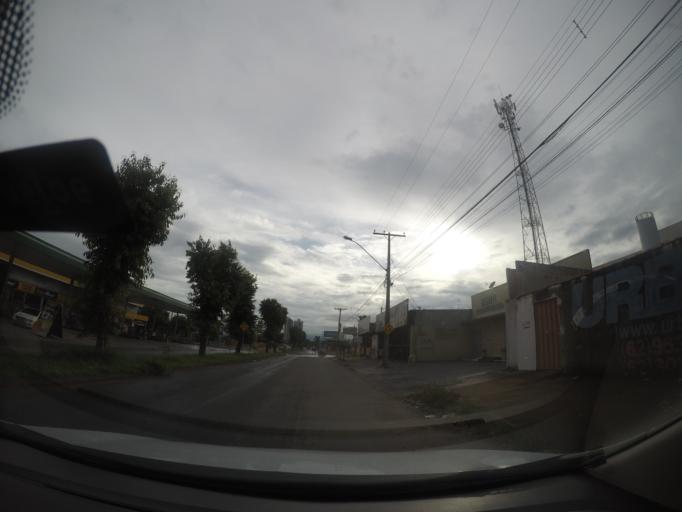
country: BR
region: Goias
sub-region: Goiania
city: Goiania
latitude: -16.7400
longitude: -49.2771
